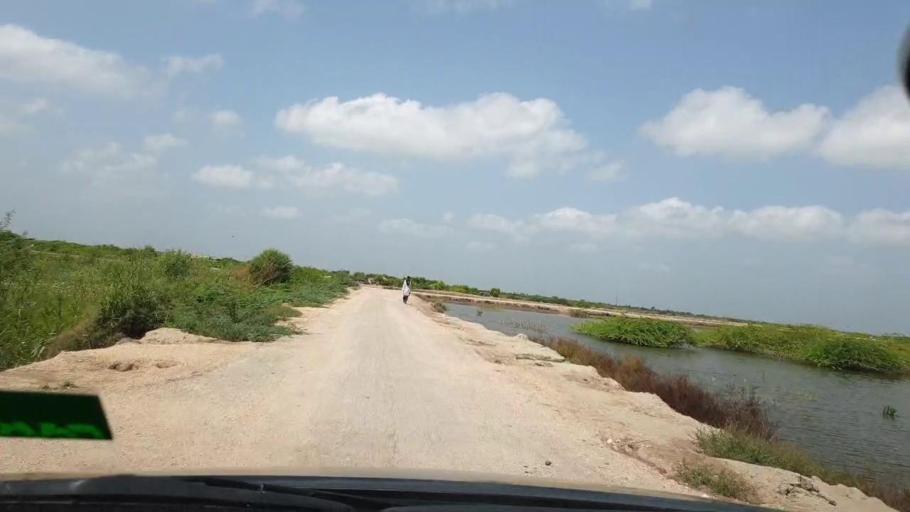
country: PK
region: Sindh
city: Kadhan
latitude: 24.5754
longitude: 69.1455
